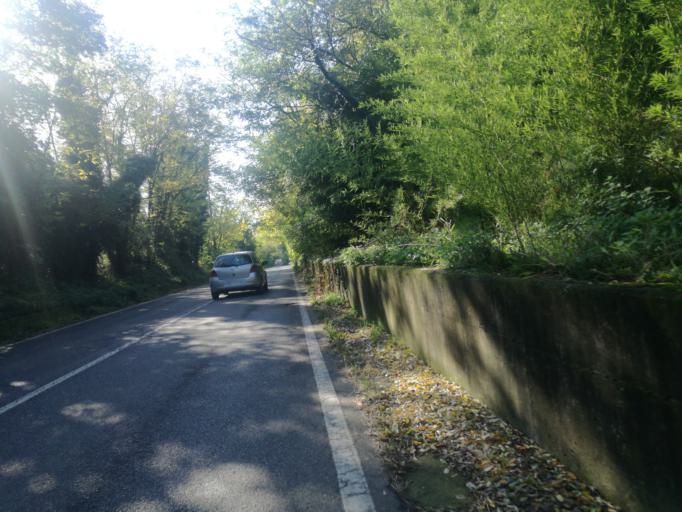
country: IT
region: Lombardy
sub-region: Provincia di Monza e Brianza
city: Cornate d'Adda
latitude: 45.6413
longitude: 9.4873
